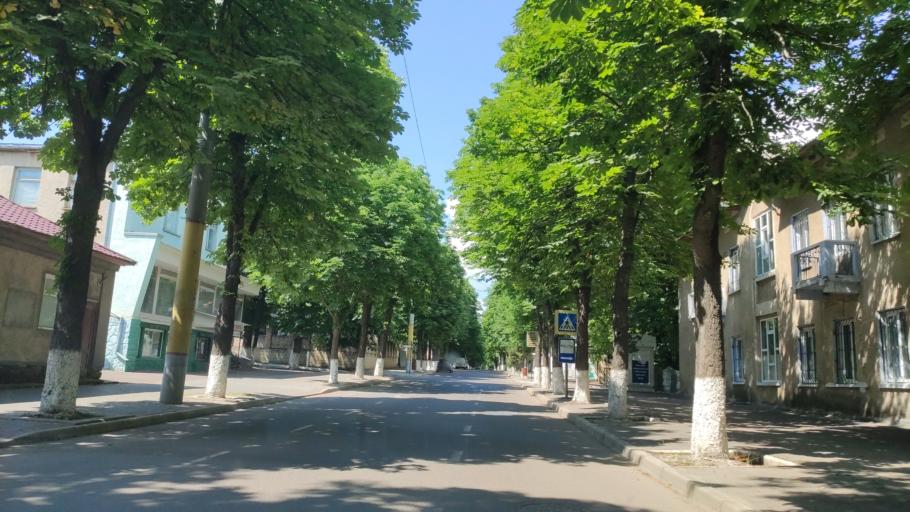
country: MD
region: Raionul Soroca
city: Soroca
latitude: 48.1511
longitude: 28.3022
